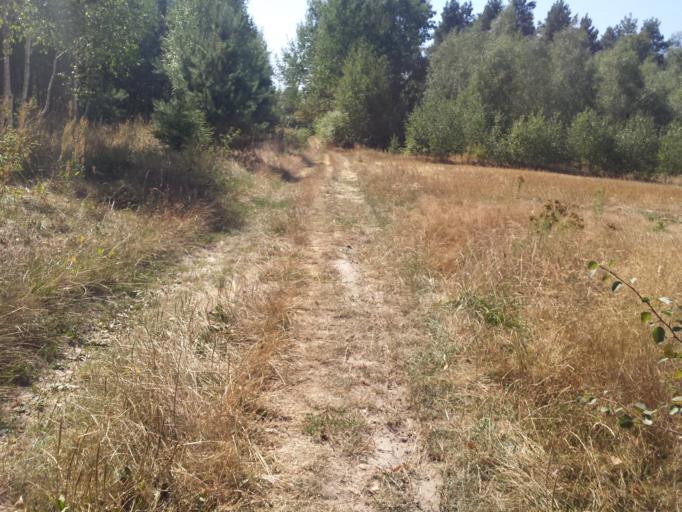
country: PL
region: Swietokrzyskie
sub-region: Powiat kielecki
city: Daleszyce
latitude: 50.8047
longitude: 20.7713
